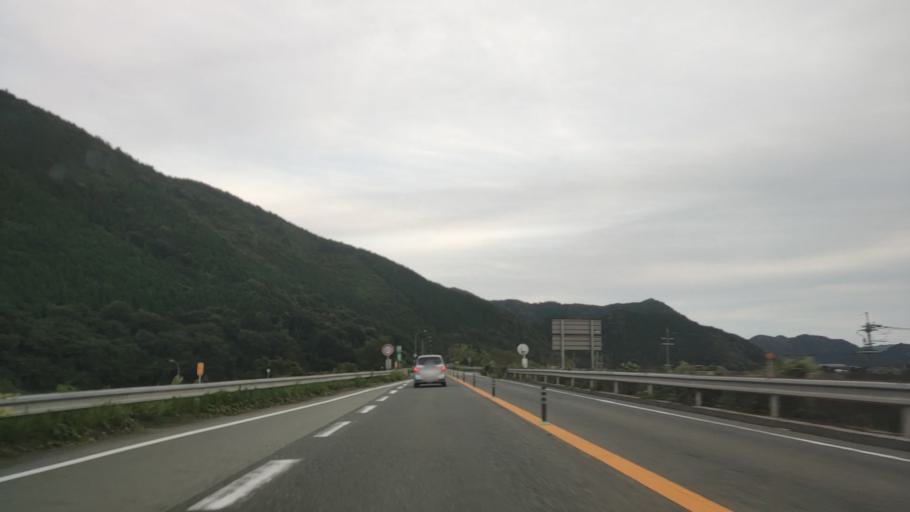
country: JP
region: Hyogo
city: Nishiwaki
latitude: 35.0450
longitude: 134.7666
